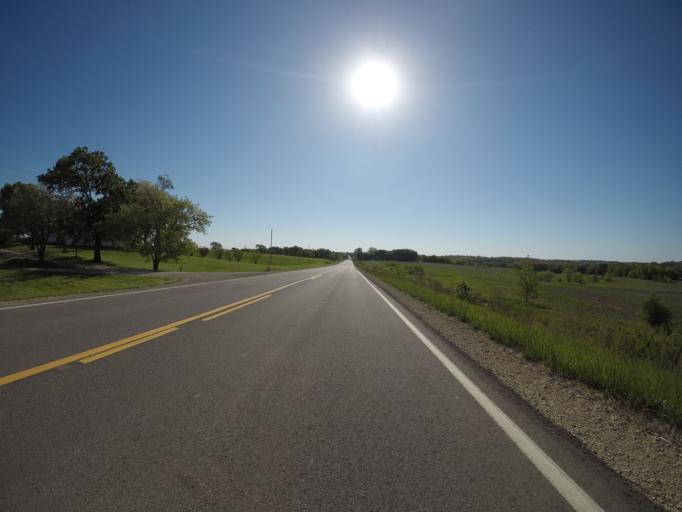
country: US
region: Kansas
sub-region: Douglas County
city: Lawrence
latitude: 39.0437
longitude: -95.4184
